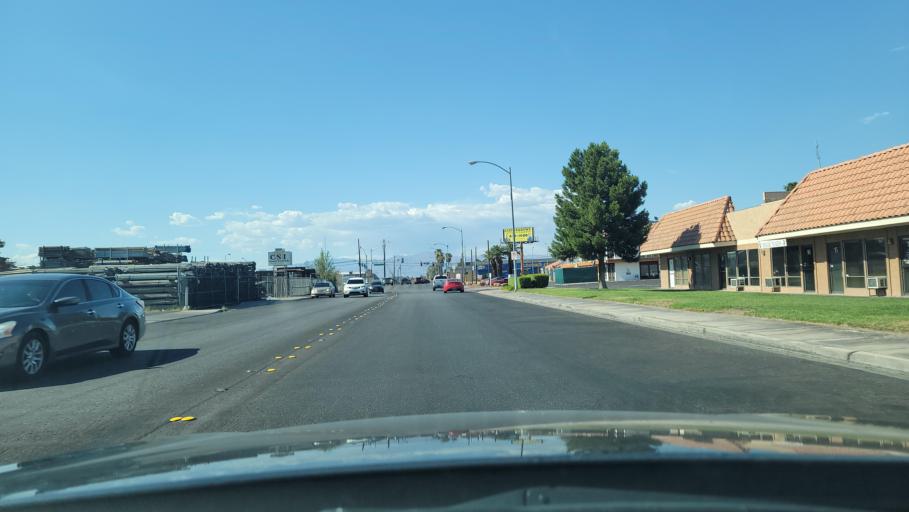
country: US
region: Nevada
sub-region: Clark County
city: Paradise
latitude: 36.1245
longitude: -115.1855
